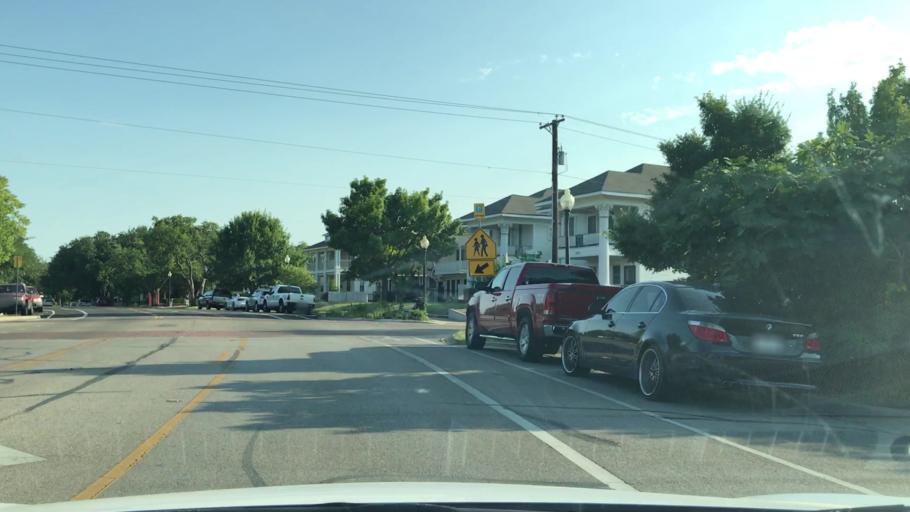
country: US
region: Texas
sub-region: Dallas County
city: Dallas
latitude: 32.7564
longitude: -96.8278
